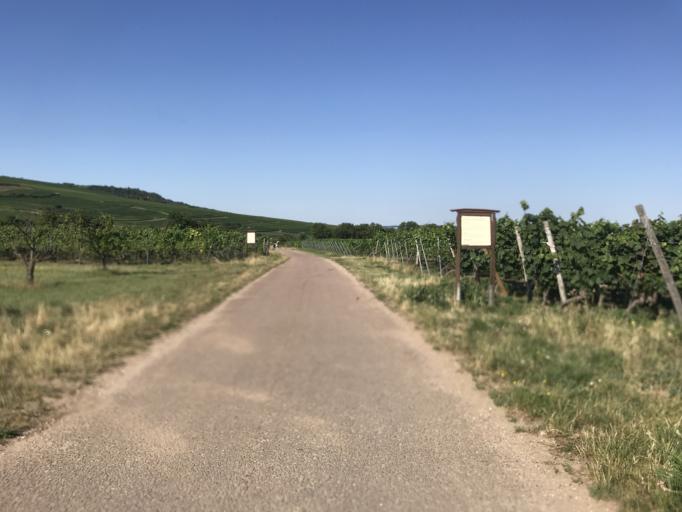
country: DE
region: Rheinland-Pfalz
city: Gau-Algesheim
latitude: 49.9538
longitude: 8.0081
